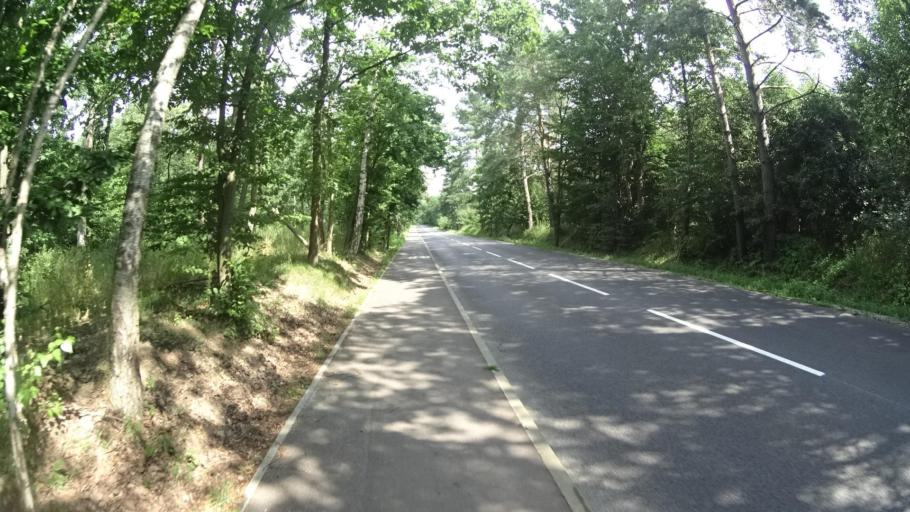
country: PL
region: Masovian Voivodeship
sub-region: Powiat piaseczynski
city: Tarczyn
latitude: 52.0260
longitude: 20.7843
